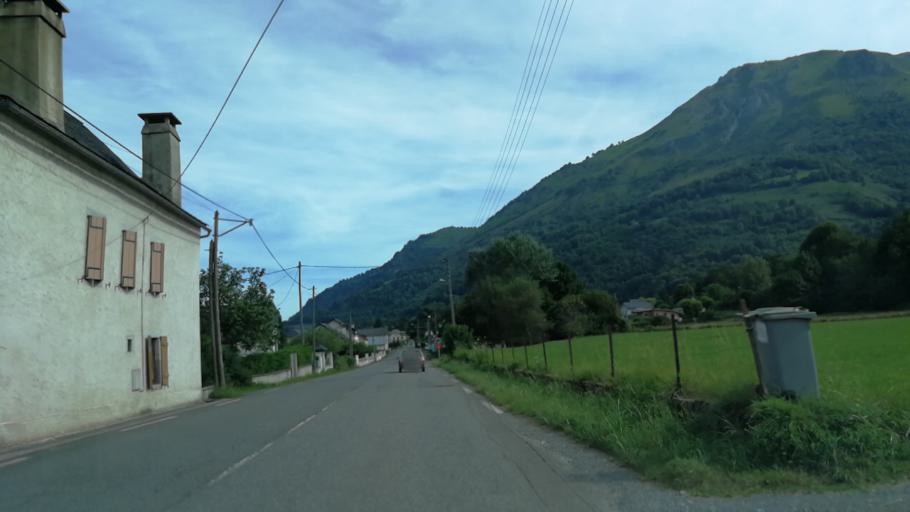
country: FR
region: Aquitaine
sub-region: Departement des Pyrenees-Atlantiques
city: Arette
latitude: 42.9904
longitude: -0.6029
